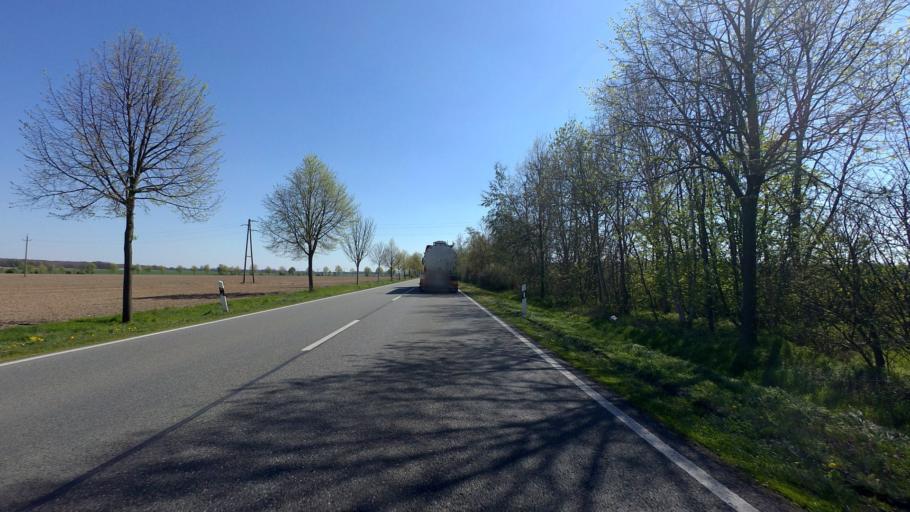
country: DE
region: Saxony-Anhalt
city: Pretzier
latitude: 52.7863
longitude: 11.2324
